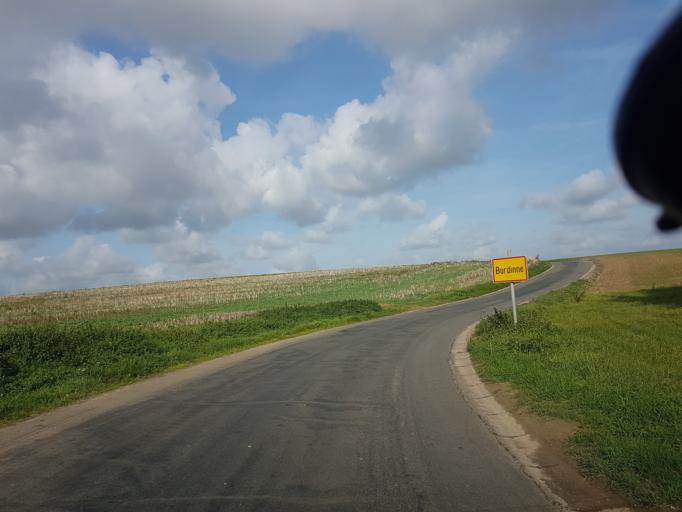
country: BE
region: Wallonia
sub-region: Province de Liege
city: Heron
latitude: 50.5644
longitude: 5.0861
